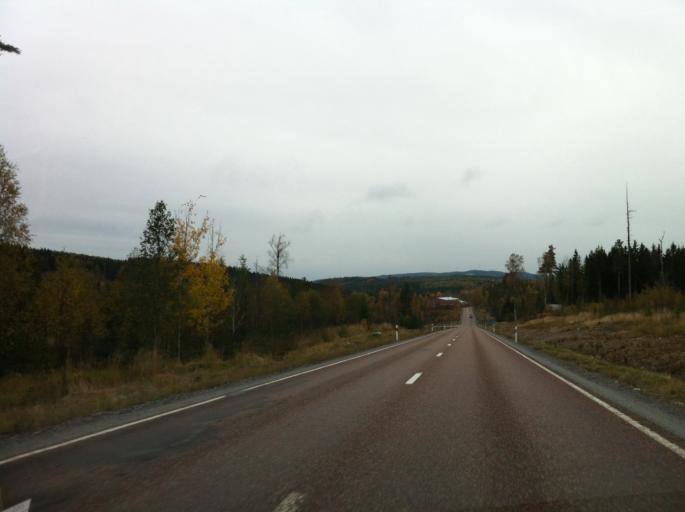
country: SE
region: Dalarna
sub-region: Ludvika Kommun
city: Grangesberg
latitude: 60.0218
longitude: 14.9816
